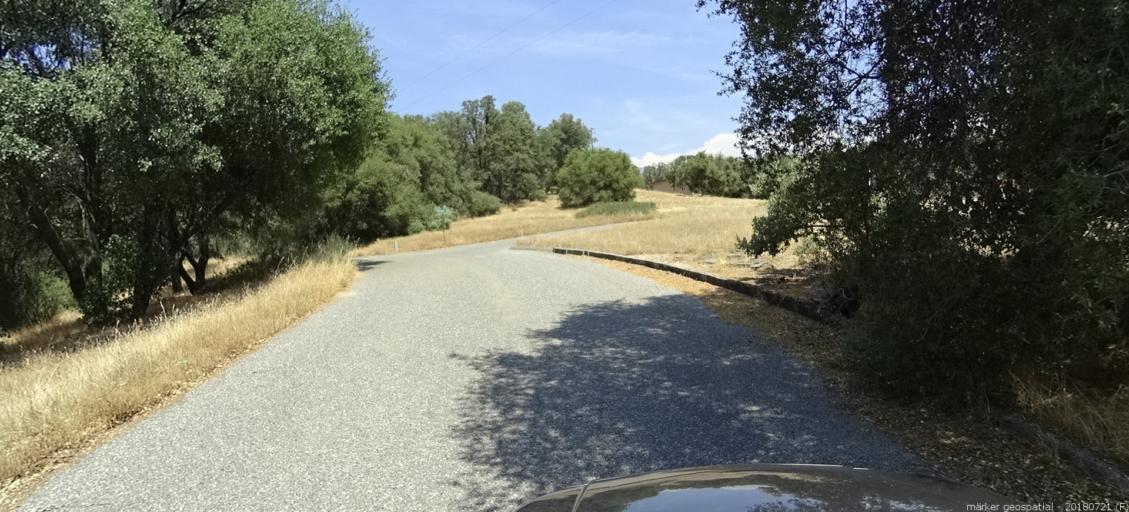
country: US
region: California
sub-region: Madera County
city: Oakhurst
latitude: 37.2242
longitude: -119.5490
